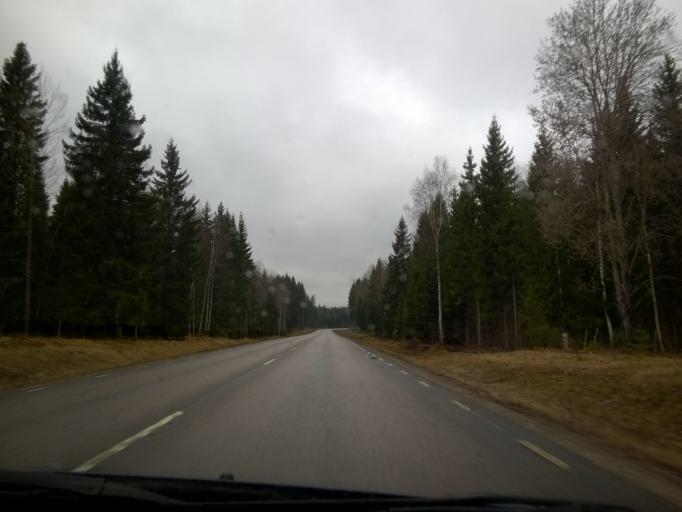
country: SE
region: Uppsala
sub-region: Osthammars Kommun
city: Bjorklinge
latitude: 60.1689
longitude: 17.5620
